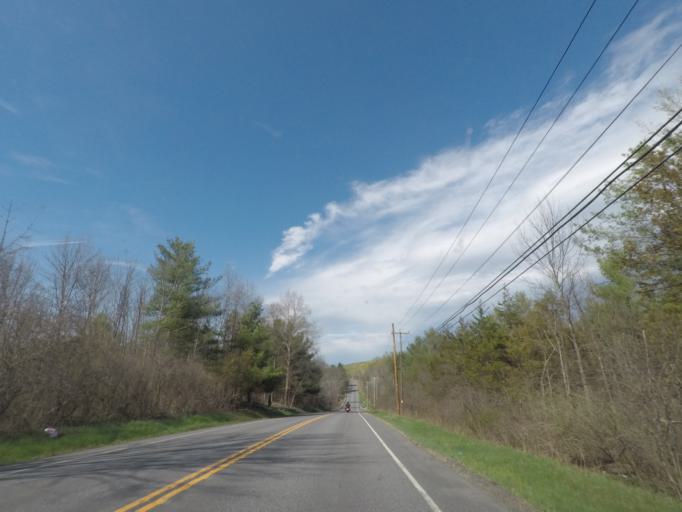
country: US
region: New York
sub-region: Greene County
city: Cairo
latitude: 42.3785
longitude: -74.0348
